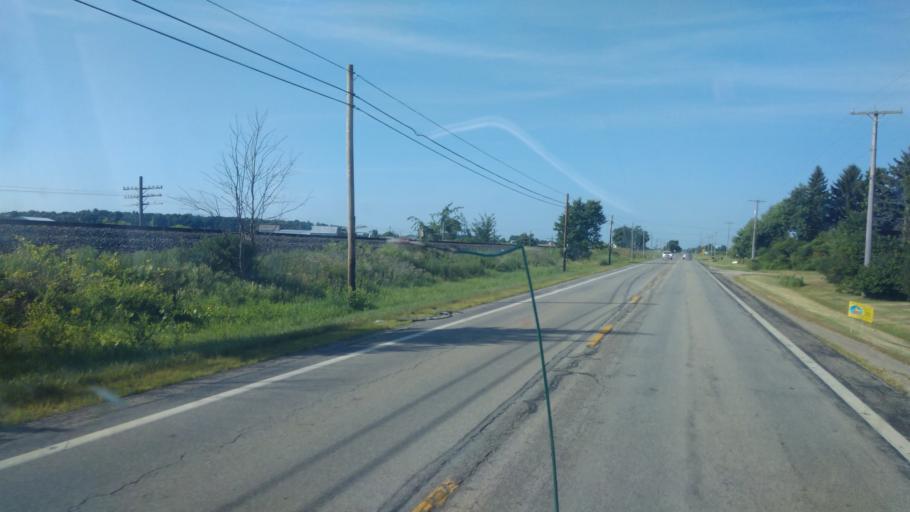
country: US
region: Ohio
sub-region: Delaware County
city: Ashley
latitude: 40.3992
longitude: -82.9621
